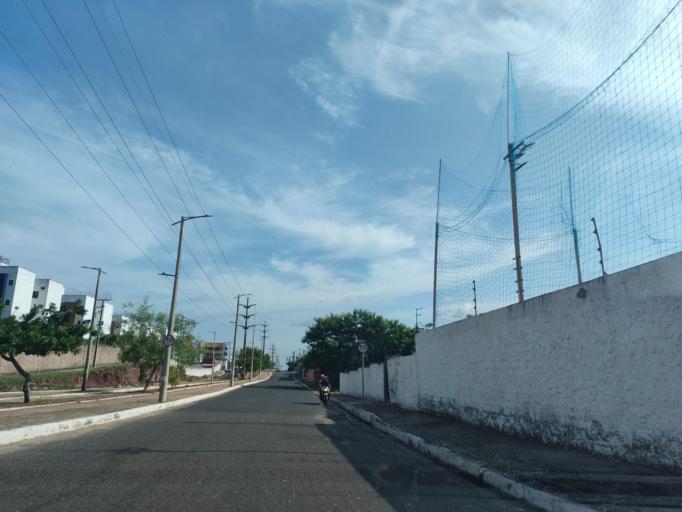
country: BR
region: Piaui
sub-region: Teresina
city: Teresina
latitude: -5.0728
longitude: -42.7516
